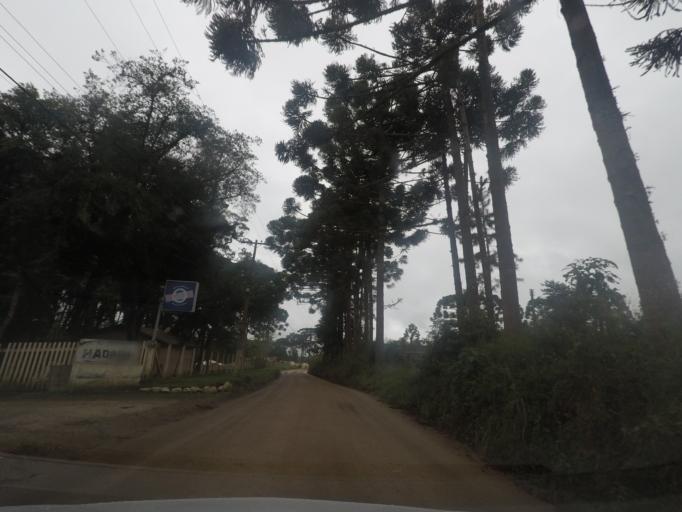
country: BR
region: Parana
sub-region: Campina Grande Do Sul
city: Campina Grande do Sul
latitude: -25.3051
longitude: -49.1173
